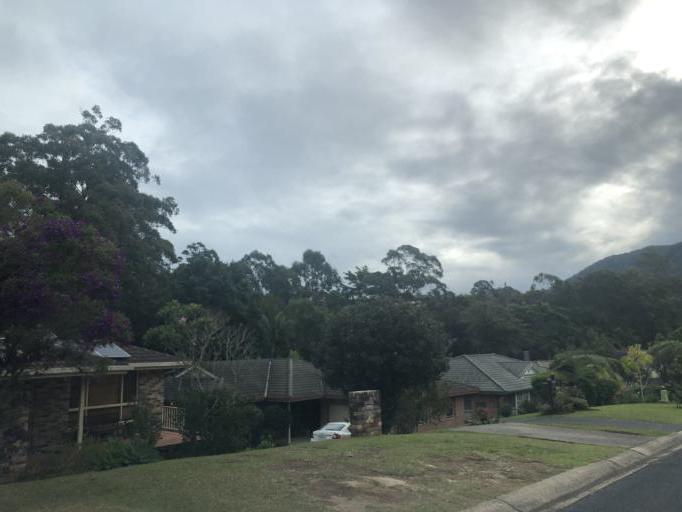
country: AU
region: New South Wales
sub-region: Coffs Harbour
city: Coffs Harbour
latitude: -30.2778
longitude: 153.1101
